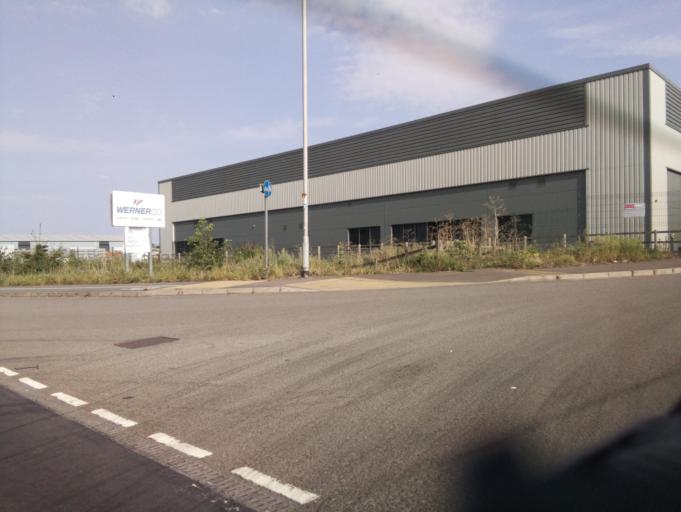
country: GB
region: England
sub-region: Staffordshire
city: Burton upon Trent
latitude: 52.8017
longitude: -1.6525
